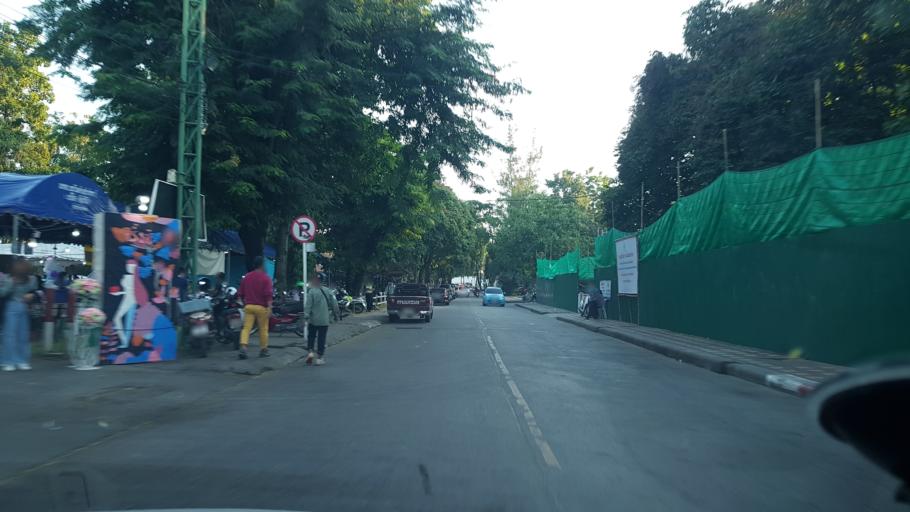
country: TH
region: Chiang Rai
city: Chiang Rai
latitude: 19.9089
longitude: 99.8352
